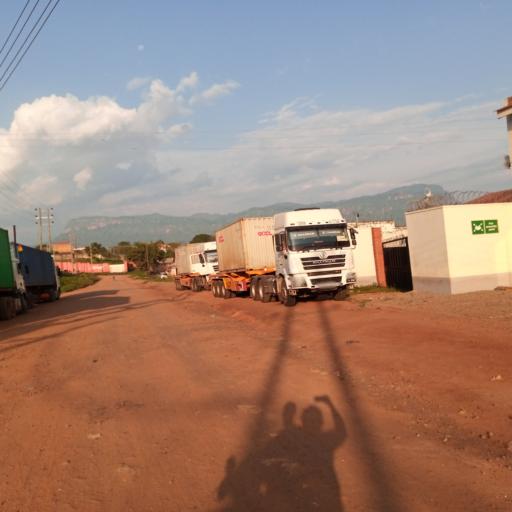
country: UG
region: Eastern Region
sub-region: Mbale District
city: Mbale
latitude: 1.0772
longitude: 34.1633
